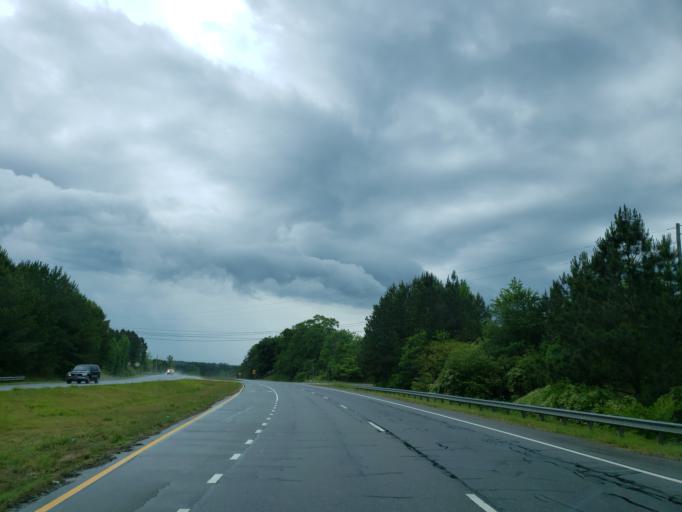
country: US
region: Georgia
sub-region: Haralson County
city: Buchanan
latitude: 33.8727
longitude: -85.2177
